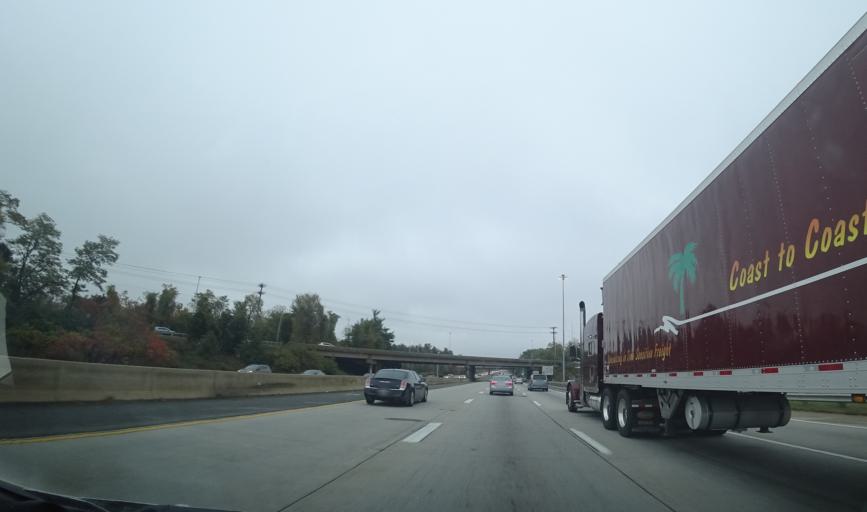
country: US
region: Virginia
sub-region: City of Fairfax
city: Fairfax
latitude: 38.8615
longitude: -77.3492
